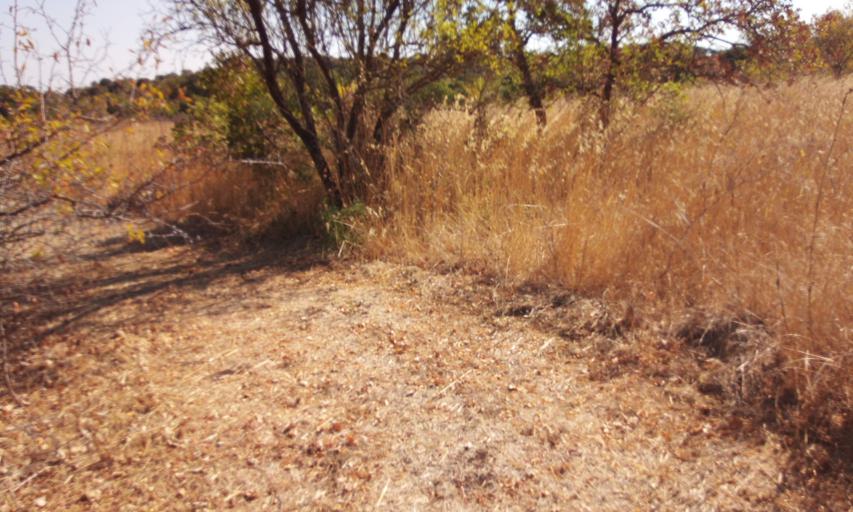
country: IT
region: Apulia
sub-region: Provincia di Bari
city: Gioia del Colle
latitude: 40.8297
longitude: 16.9607
